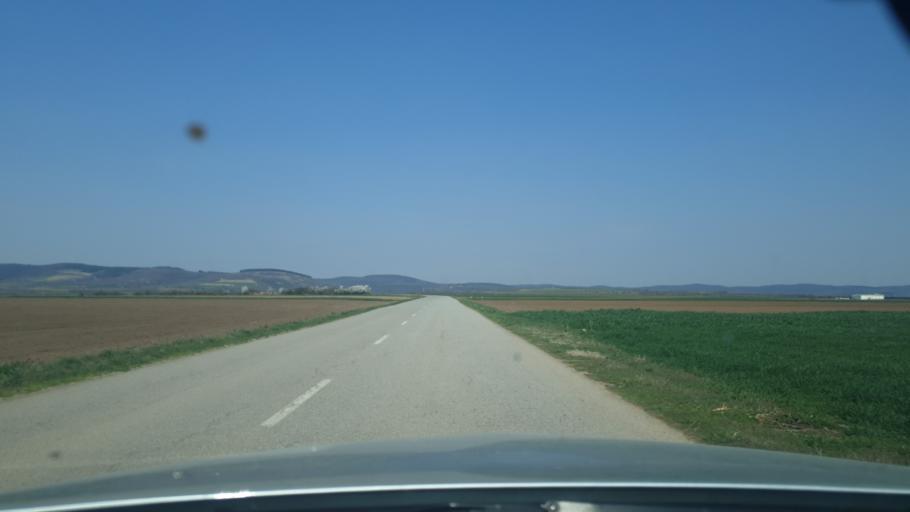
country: RS
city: Vrdnik
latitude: 45.0802
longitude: 19.7698
